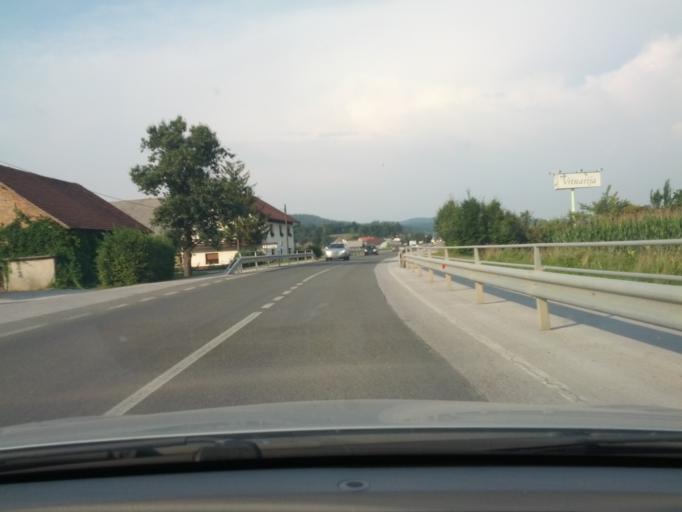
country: SI
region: Vrhnika
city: Verd
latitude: 45.9893
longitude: 14.3209
